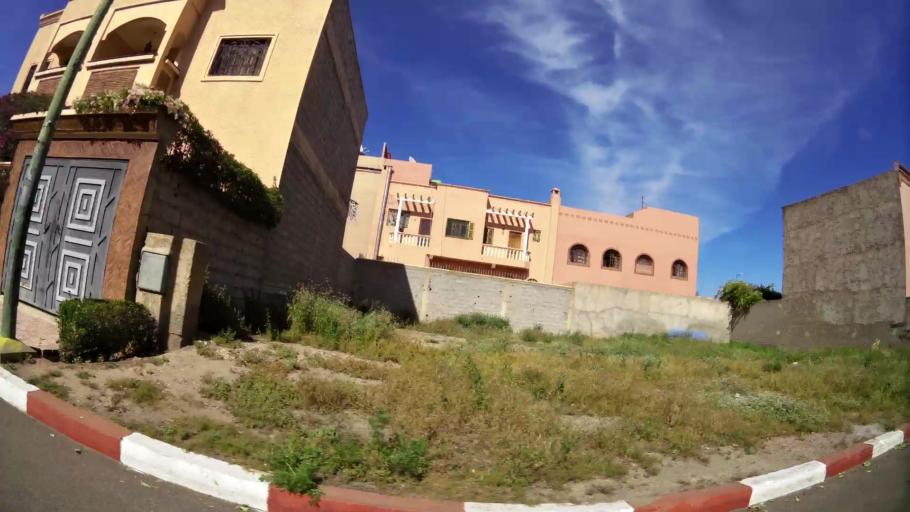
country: MA
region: Marrakech-Tensift-Al Haouz
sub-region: Marrakech
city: Marrakesh
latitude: 31.6494
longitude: -8.0490
